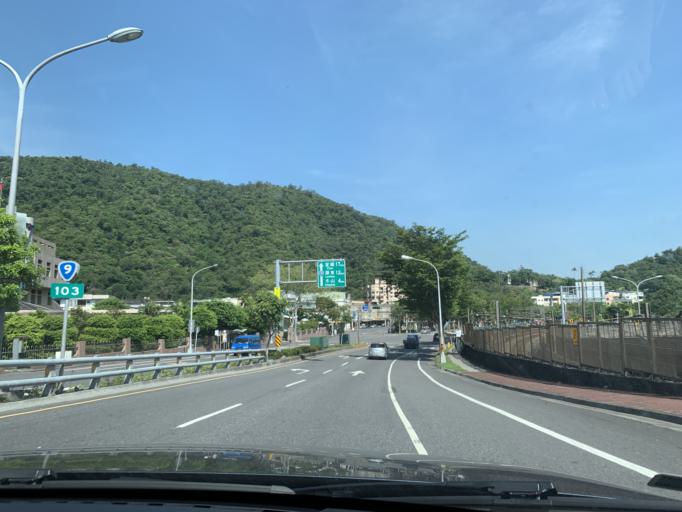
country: TW
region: Taiwan
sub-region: Yilan
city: Yilan
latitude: 24.5967
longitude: 121.8356
